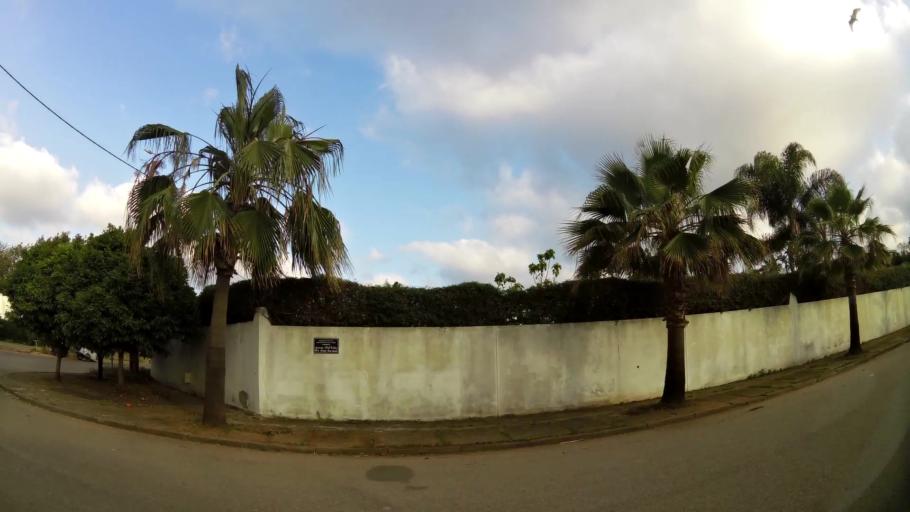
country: MA
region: Rabat-Sale-Zemmour-Zaer
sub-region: Rabat
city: Rabat
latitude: 33.9658
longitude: -6.8465
